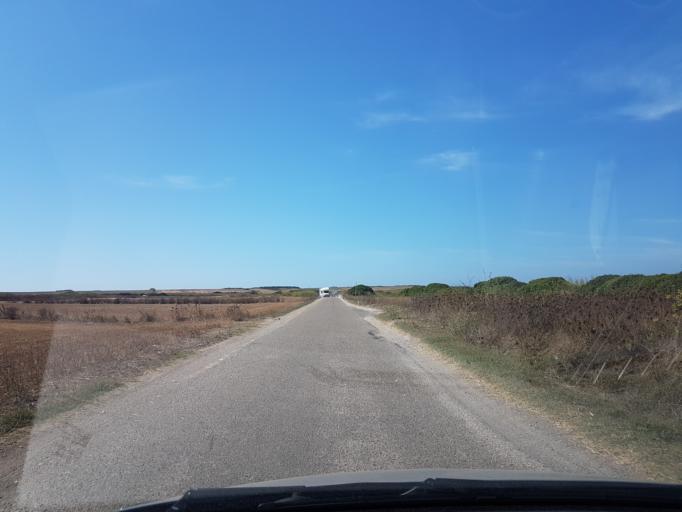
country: IT
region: Sardinia
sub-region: Provincia di Oristano
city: Nurachi
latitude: 39.9735
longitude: 8.4204
